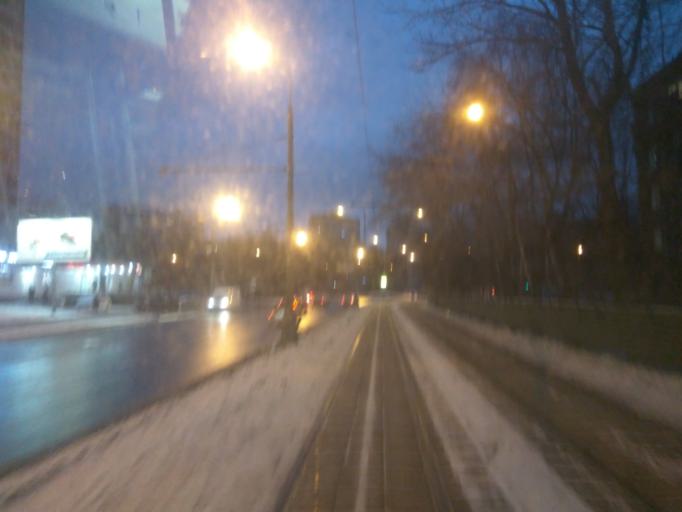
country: RU
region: Moskovskaya
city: Novogireyevo
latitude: 55.7536
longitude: 37.7994
